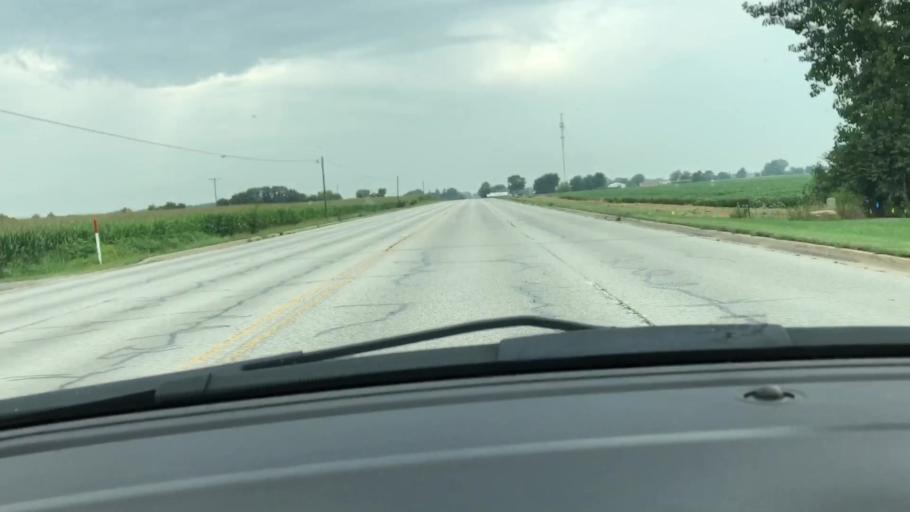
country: US
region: Michigan
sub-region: Saginaw County
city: Shields
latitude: 43.4810
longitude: -84.0615
